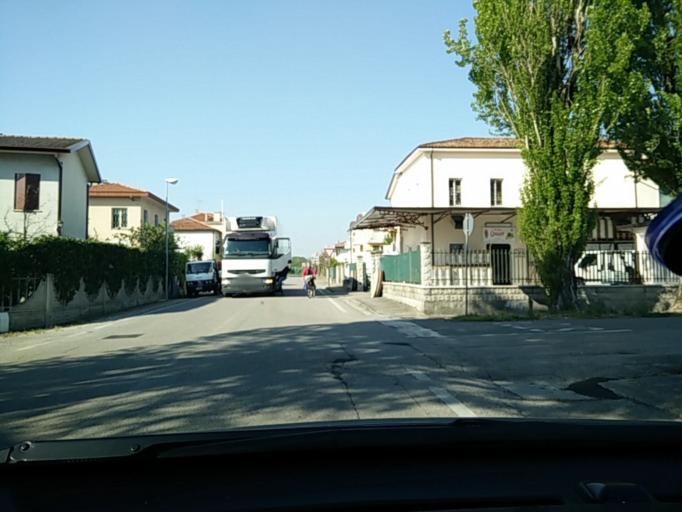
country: IT
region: Veneto
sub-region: Provincia di Venezia
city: Musile di Piave
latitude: 45.6207
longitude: 12.5566
